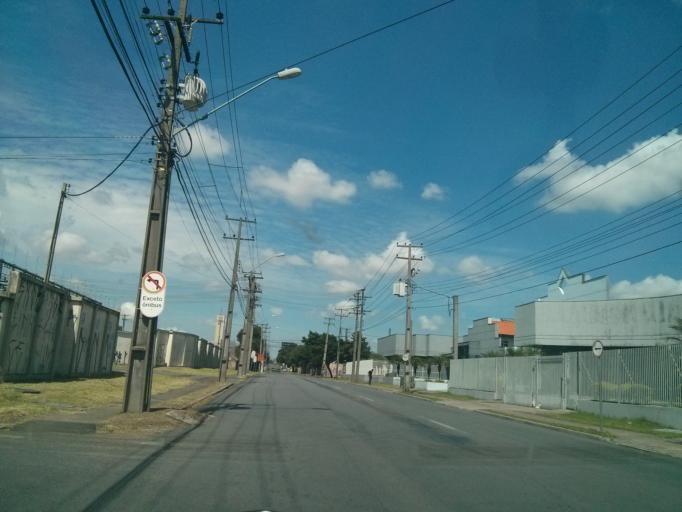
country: BR
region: Parana
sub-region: Sao Jose Dos Pinhais
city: Sao Jose dos Pinhais
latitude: -25.5219
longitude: -49.2288
